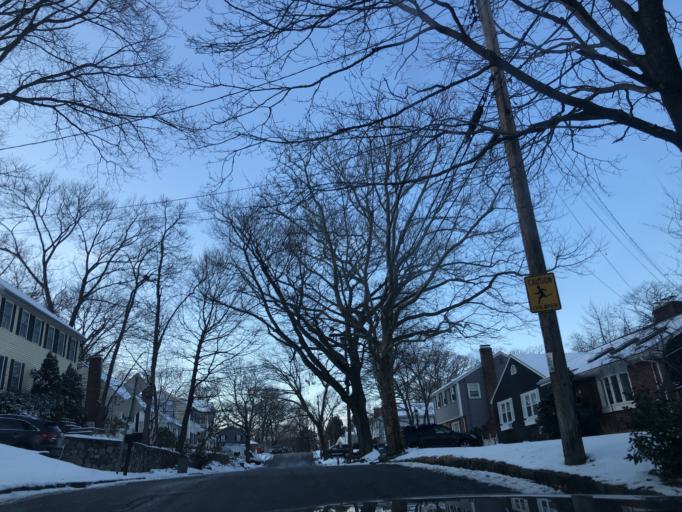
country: US
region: Massachusetts
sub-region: Middlesex County
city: Arlington
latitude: 42.4252
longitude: -71.1601
